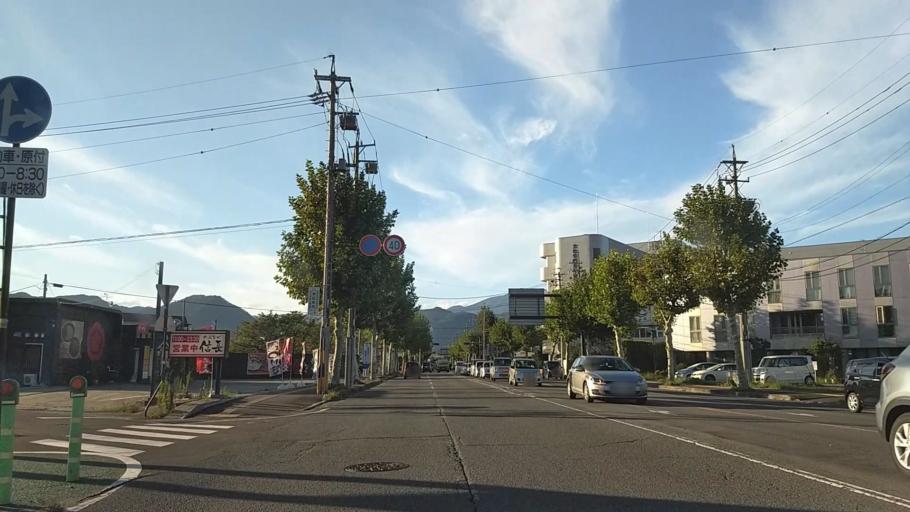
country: JP
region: Nagano
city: Nagano-shi
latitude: 36.6310
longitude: 138.2034
